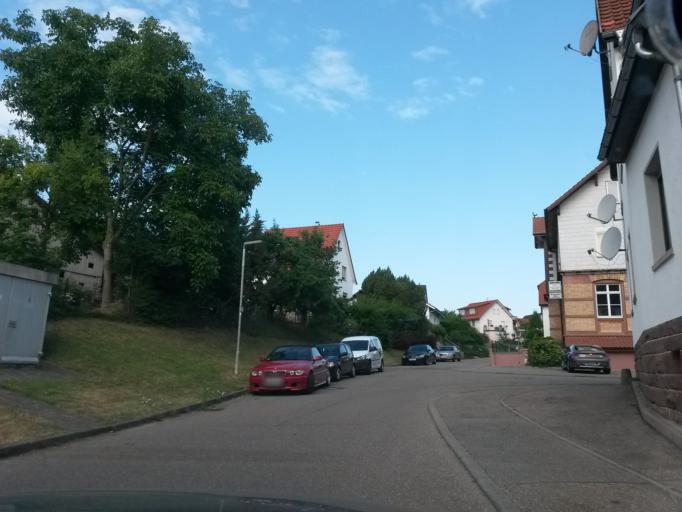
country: DE
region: Baden-Wuerttemberg
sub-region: Karlsruhe Region
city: Birkenfeld
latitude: 48.8960
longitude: 8.6000
